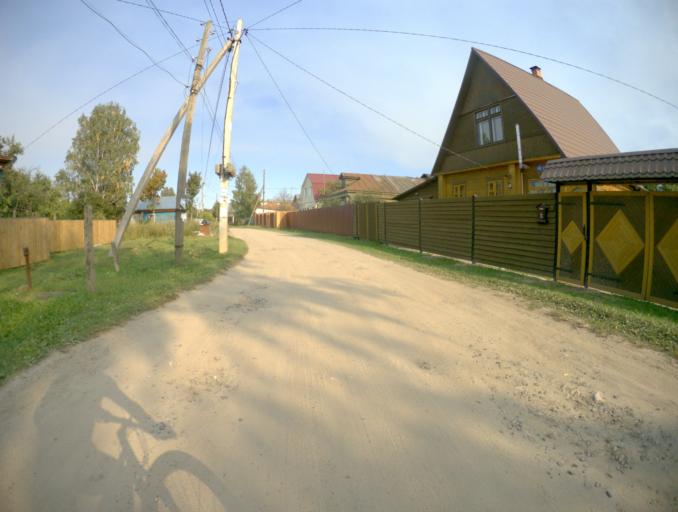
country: RU
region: Vladimir
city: Kosterevo
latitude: 55.9272
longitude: 39.5989
